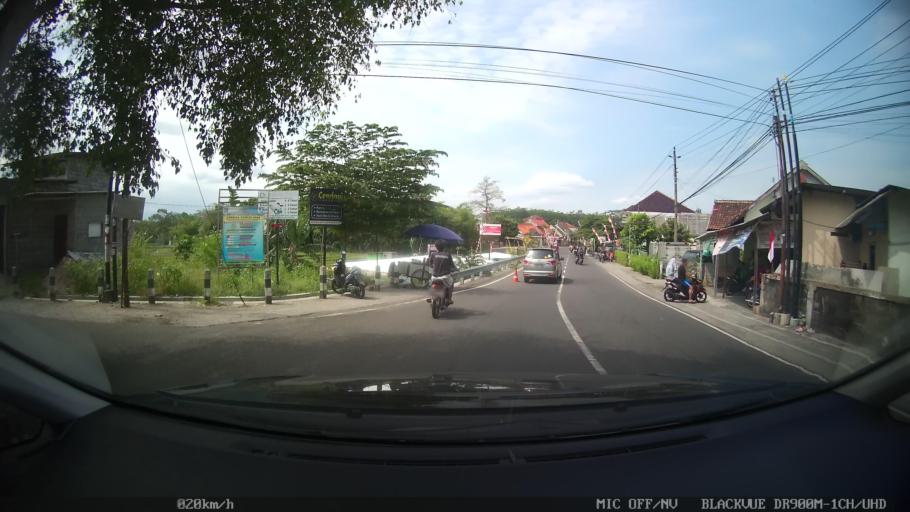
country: ID
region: Daerah Istimewa Yogyakarta
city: Depok
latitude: -7.7733
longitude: 110.4359
